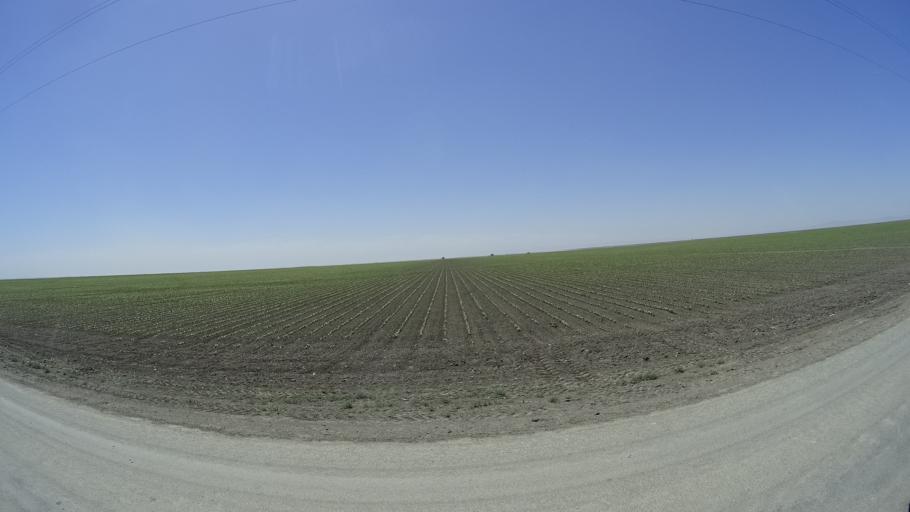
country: US
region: California
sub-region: Kings County
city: Corcoran
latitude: 36.0213
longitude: -119.6848
